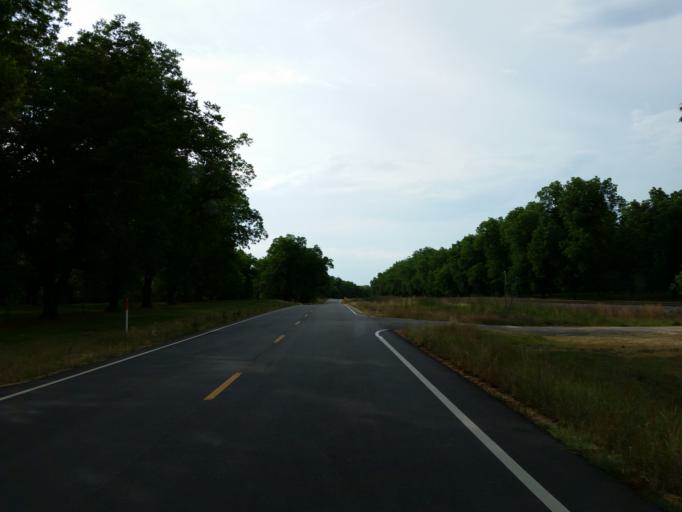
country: US
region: Georgia
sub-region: Turner County
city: Ashburn
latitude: 31.7867
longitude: -83.7026
